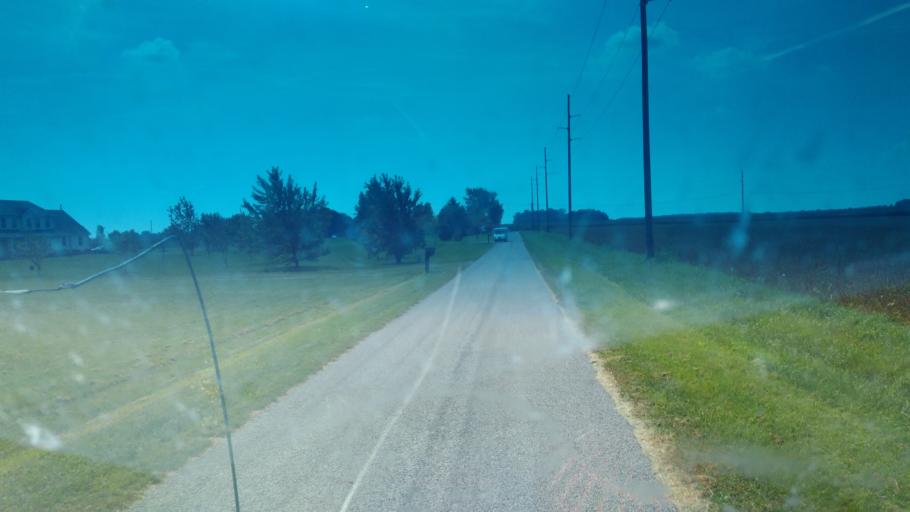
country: US
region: Ohio
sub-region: Union County
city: Richwood
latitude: 40.6029
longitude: -83.3240
